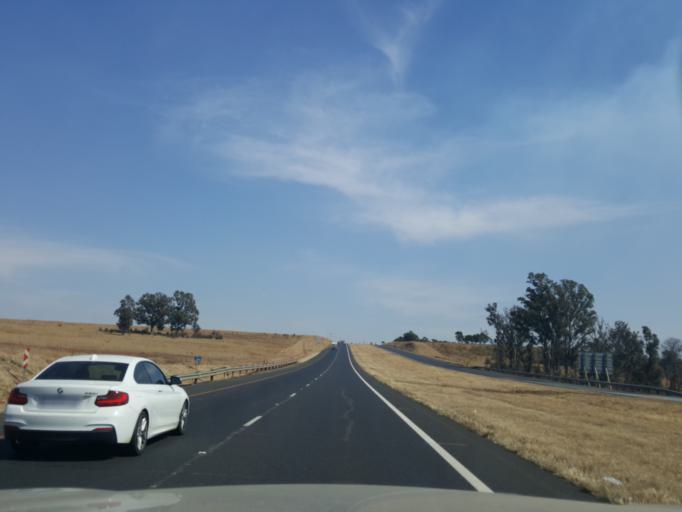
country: ZA
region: Mpumalanga
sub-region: Nkangala District Municipality
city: Witbank
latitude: -25.8716
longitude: 29.3546
